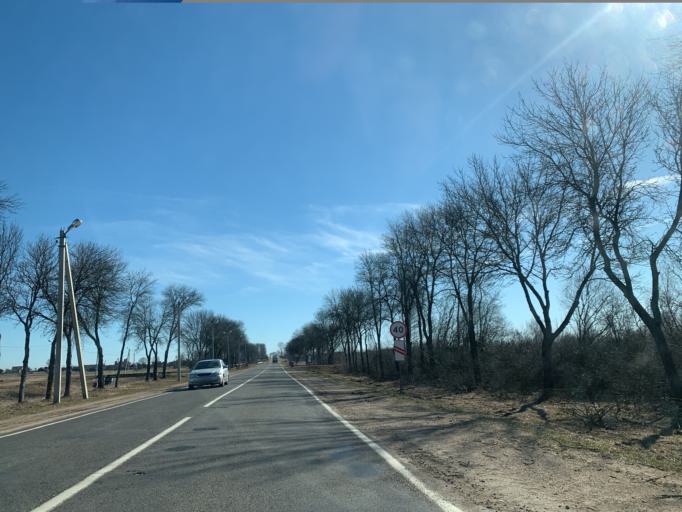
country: BY
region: Minsk
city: Nyasvizh
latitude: 53.2289
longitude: 26.7412
